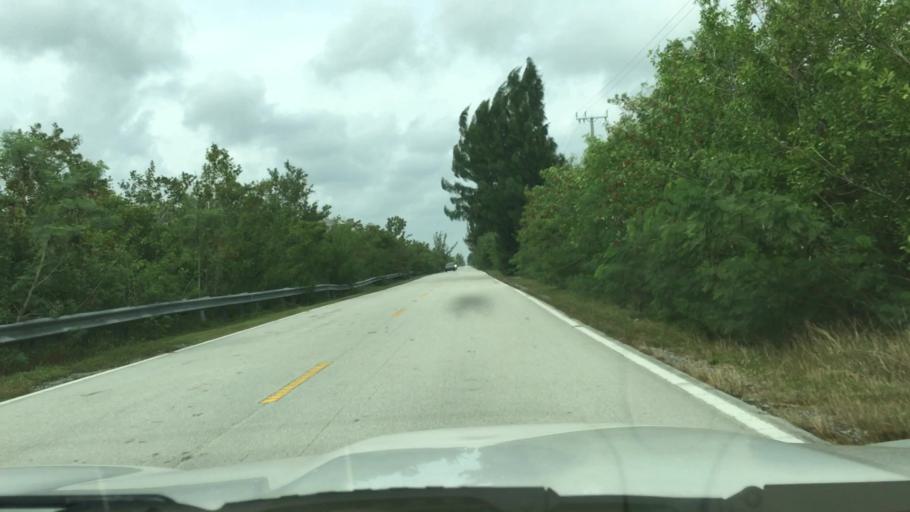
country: US
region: Florida
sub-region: Monroe County
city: North Key Largo
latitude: 25.3374
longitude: -80.4106
